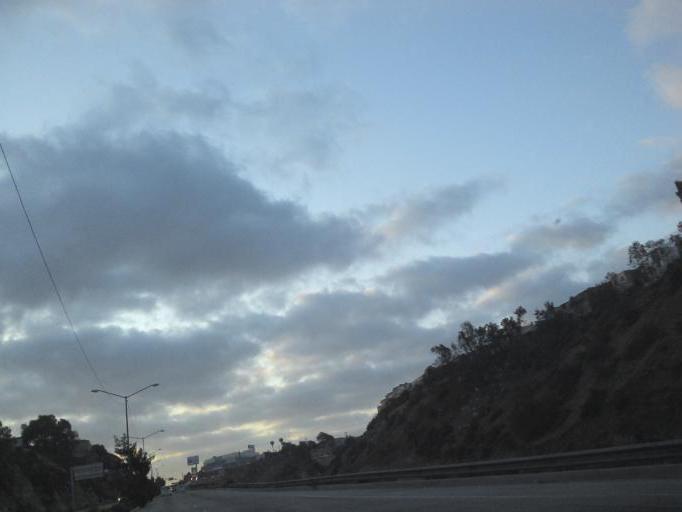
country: US
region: California
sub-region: San Diego County
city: Imperial Beach
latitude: 32.5319
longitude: -117.0818
